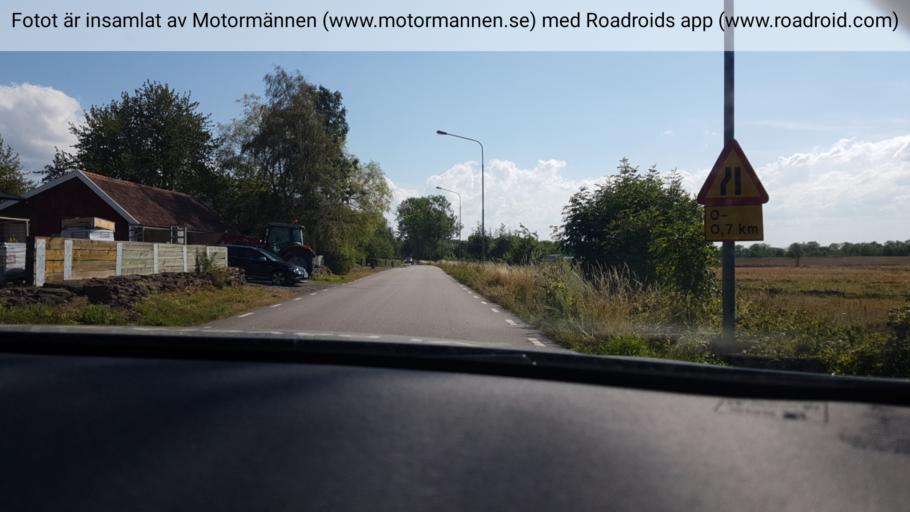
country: SE
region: Vaestra Goetaland
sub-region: Gotene Kommun
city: Kallby
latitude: 58.5631
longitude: 13.3515
